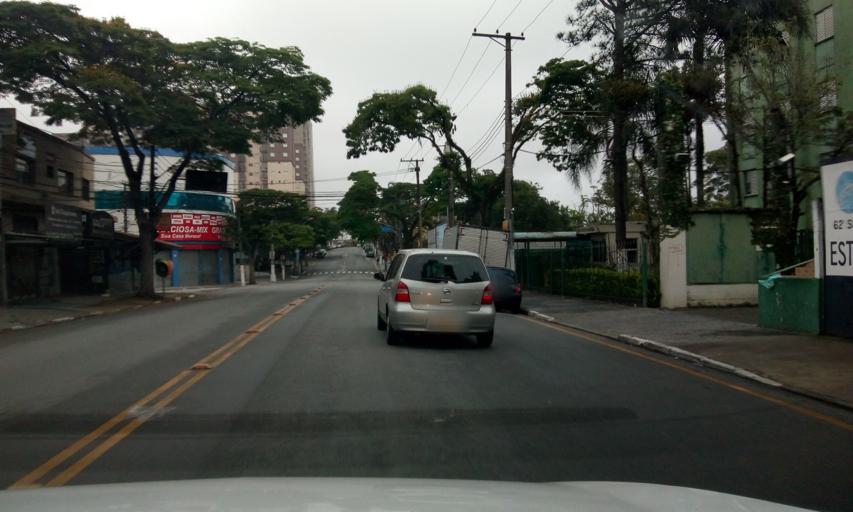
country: BR
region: Sao Paulo
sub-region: Diadema
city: Diadema
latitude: -23.6917
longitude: -46.6188
